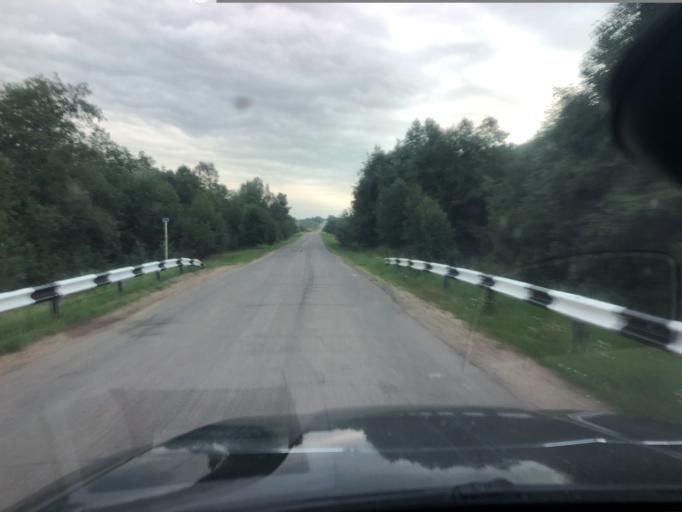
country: RU
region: Jaroslavl
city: Petrovsk
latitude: 57.0136
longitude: 38.9948
